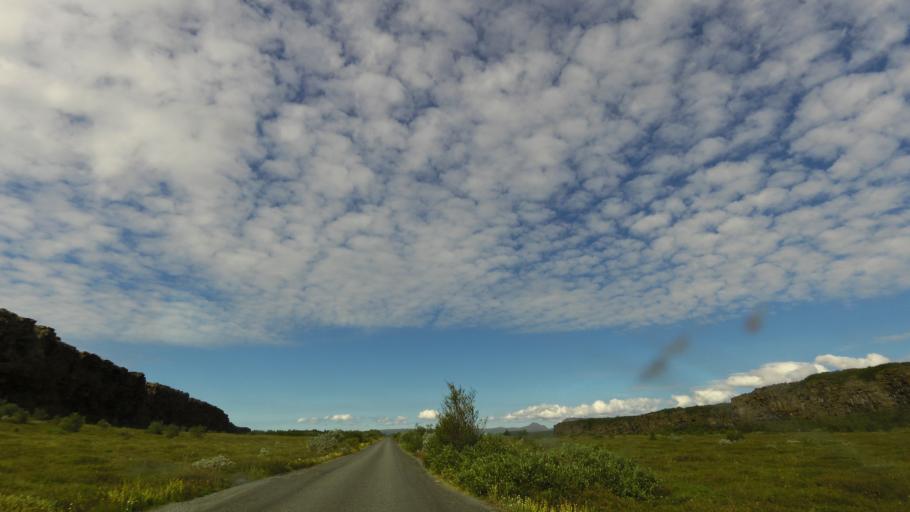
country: IS
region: Northeast
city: Husavik
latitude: 66.0181
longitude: -16.4971
